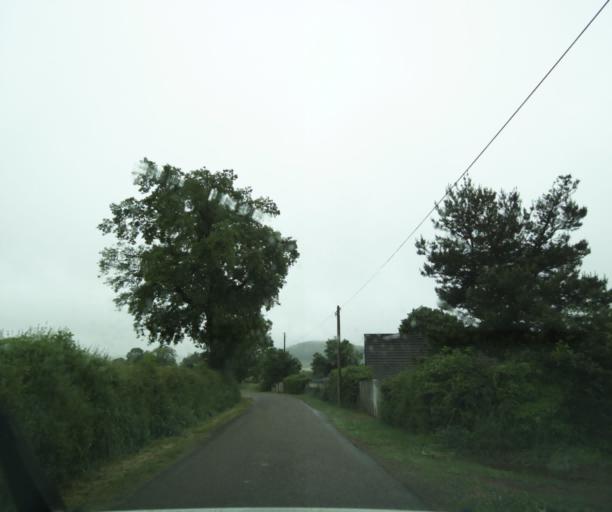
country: FR
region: Bourgogne
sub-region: Departement de Saone-et-Loire
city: Charolles
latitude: 46.4048
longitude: 4.3738
